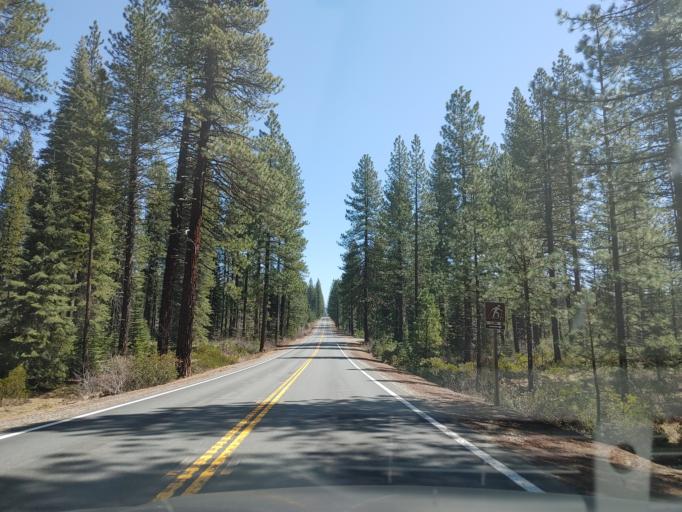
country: US
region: California
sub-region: Siskiyou County
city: McCloud
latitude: 41.2665
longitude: -121.8812
